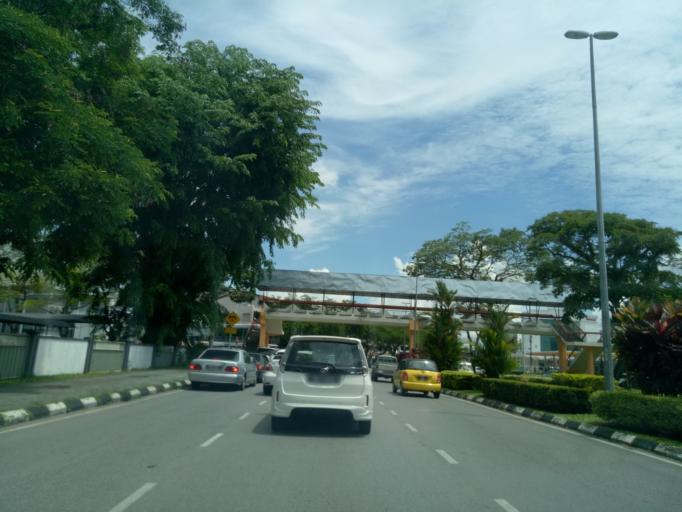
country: MY
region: Sarawak
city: Kuching
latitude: 1.5524
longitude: 110.3615
